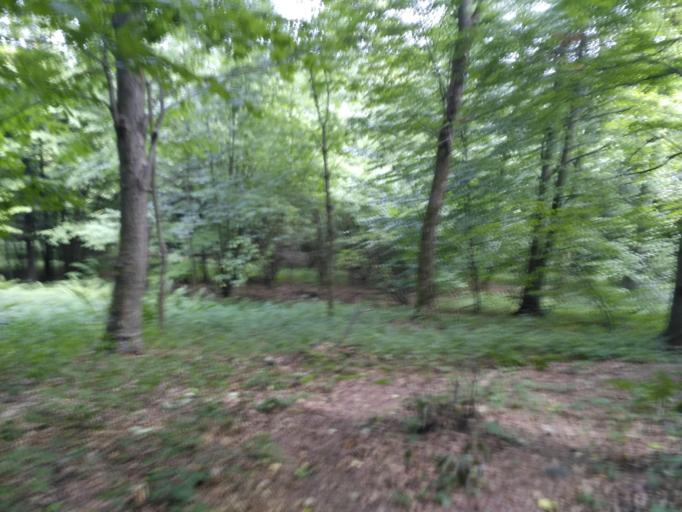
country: PL
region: Subcarpathian Voivodeship
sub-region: Powiat strzyzowski
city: Frysztak
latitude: 49.8858
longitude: 21.5463
